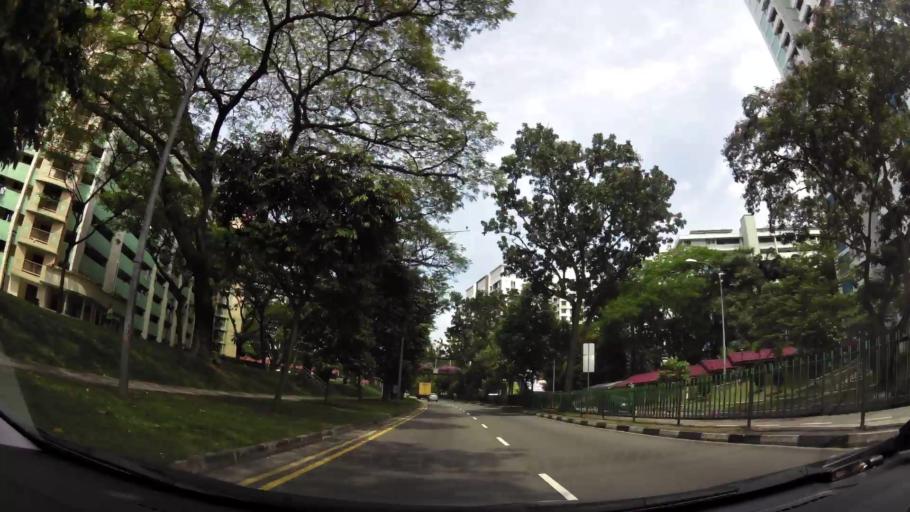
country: MY
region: Johor
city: Johor Bahru
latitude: 1.3465
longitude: 103.7157
